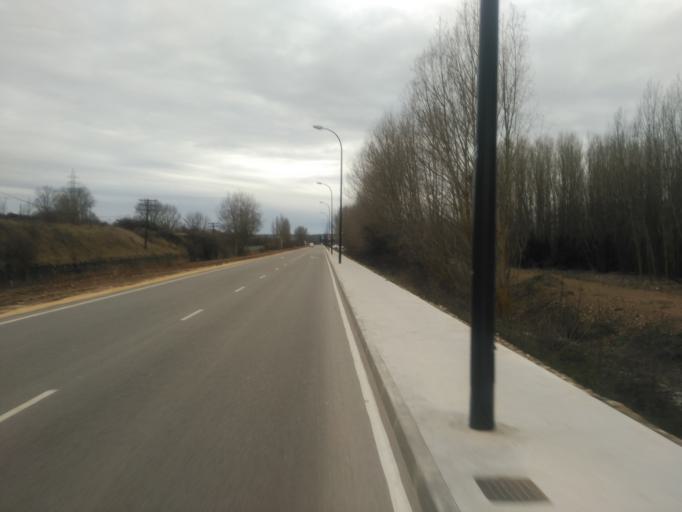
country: ES
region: Castille and Leon
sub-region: Provincia de Burgos
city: Villagonzalo-Pedernales
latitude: 42.3349
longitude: -3.7242
